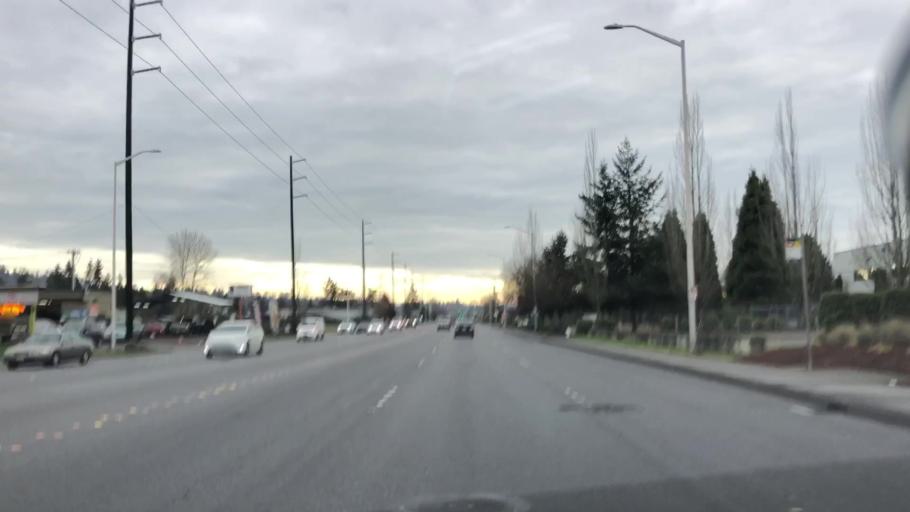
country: US
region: Washington
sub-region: King County
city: Kent
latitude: 47.4080
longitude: -122.2281
